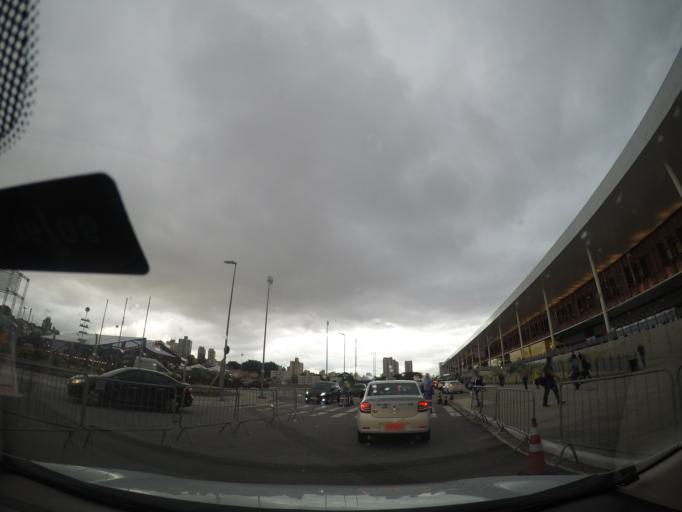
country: BR
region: Sao Paulo
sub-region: Diadema
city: Diadema
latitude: -23.6476
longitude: -46.6303
